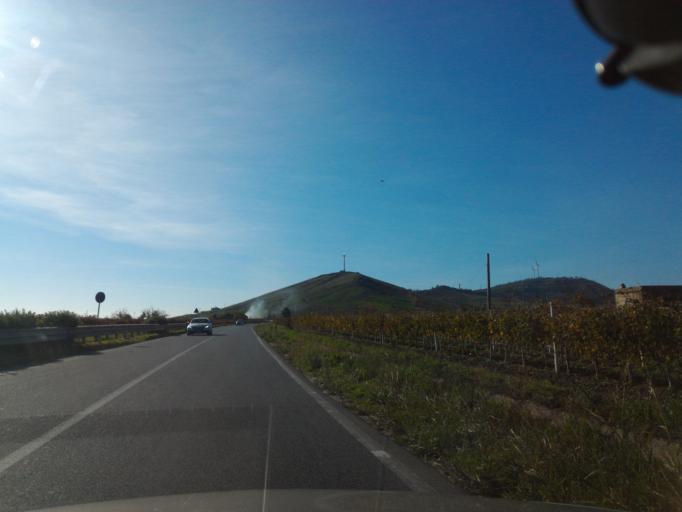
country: IT
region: Calabria
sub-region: Provincia di Crotone
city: Ciro Marina
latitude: 39.3452
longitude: 17.1078
